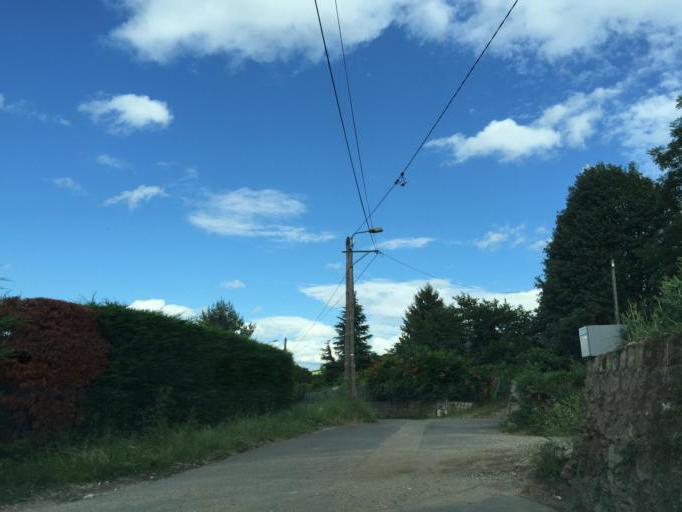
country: FR
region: Rhone-Alpes
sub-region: Departement de la Loire
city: Saint-Jean-Bonnefonds
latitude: 45.4404
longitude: 4.4724
